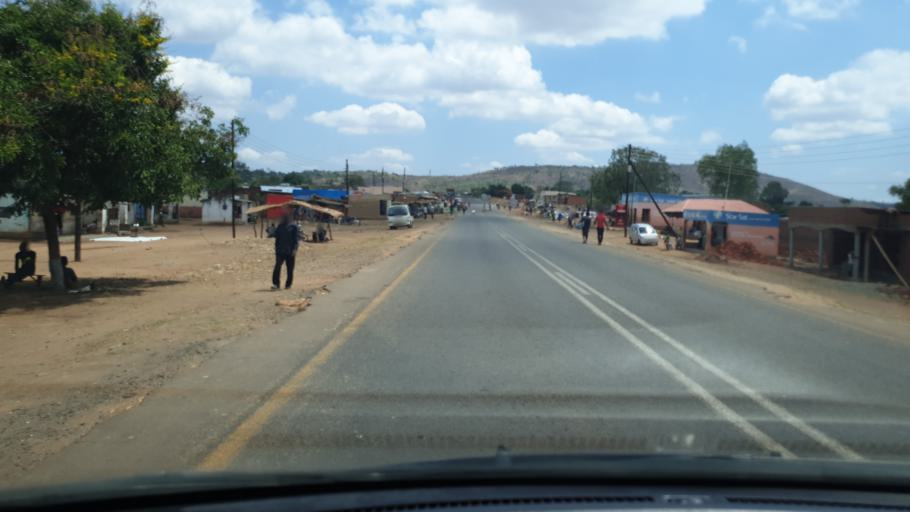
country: MW
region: Central Region
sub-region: Dowa District
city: Dowa
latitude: -13.7661
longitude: 34.0135
